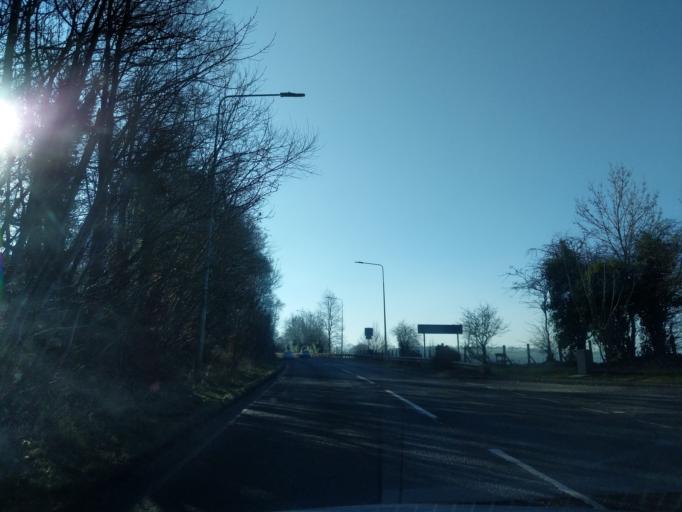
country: GB
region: Scotland
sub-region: South Lanarkshire
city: Lanark
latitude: 55.6794
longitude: -3.7959
